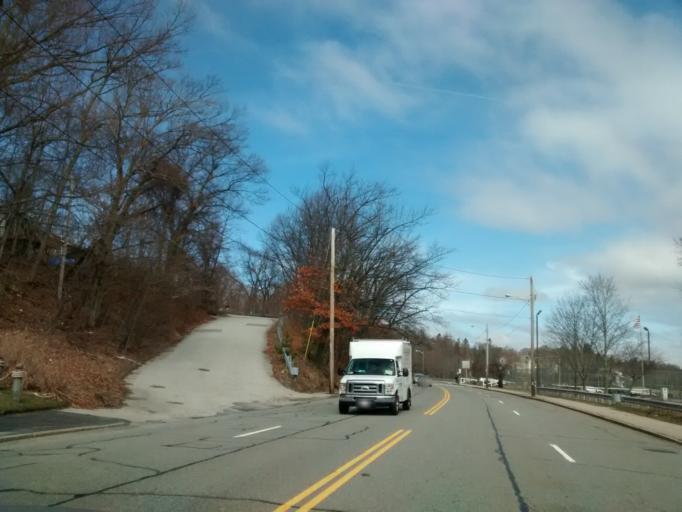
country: US
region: Massachusetts
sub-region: Worcester County
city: Worcester
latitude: 42.2920
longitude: -71.8163
